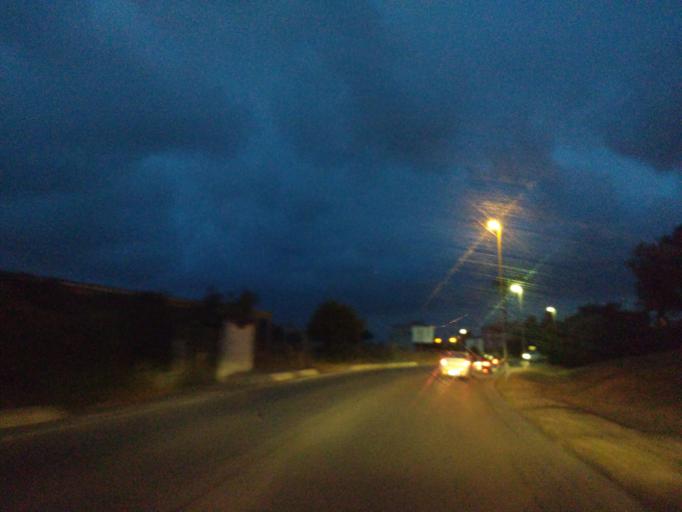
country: IT
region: Latium
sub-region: Citta metropolitana di Roma Capitale
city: Anzio
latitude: 41.4553
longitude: 12.6215
